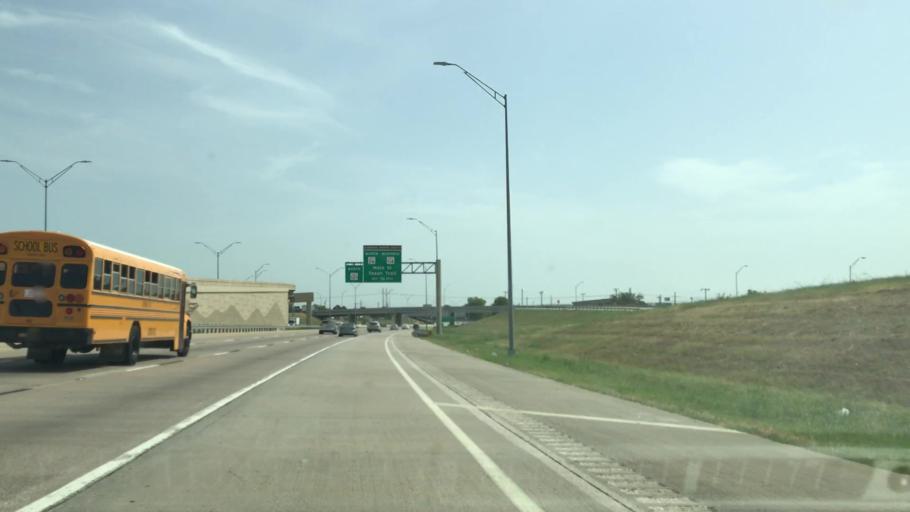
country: US
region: Texas
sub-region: Tarrant County
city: Grapevine
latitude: 32.9167
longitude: -97.0950
